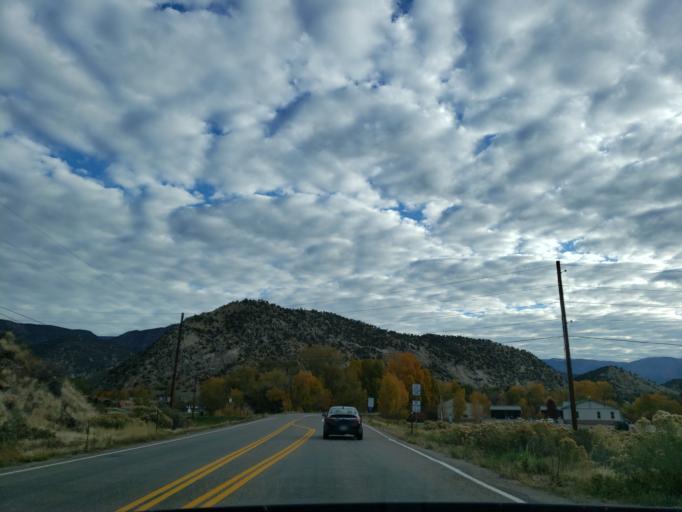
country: US
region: Colorado
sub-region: Garfield County
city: New Castle
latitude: 39.5700
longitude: -107.5430
